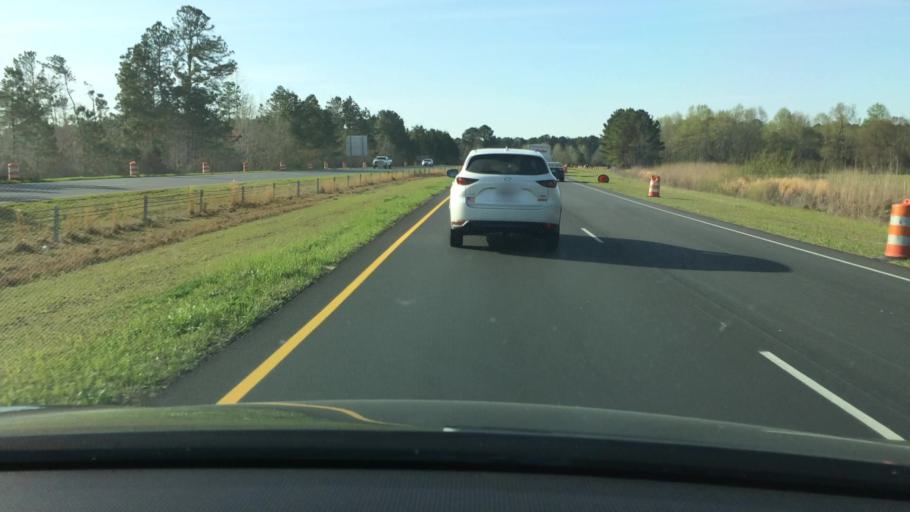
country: US
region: North Carolina
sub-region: Johnston County
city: Pine Level
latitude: 35.4970
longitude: -78.2777
